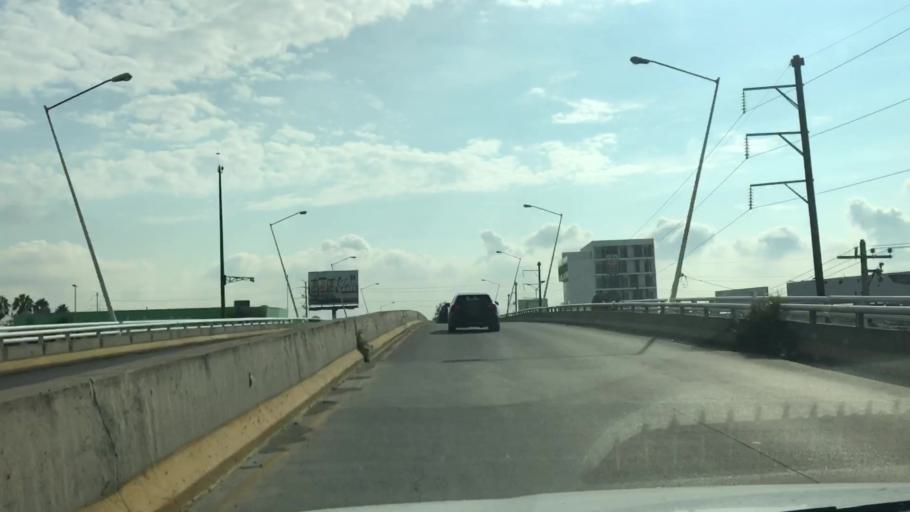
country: MX
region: Jalisco
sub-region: Tlajomulco de Zuniga
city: Palomar
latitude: 20.6307
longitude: -103.4368
